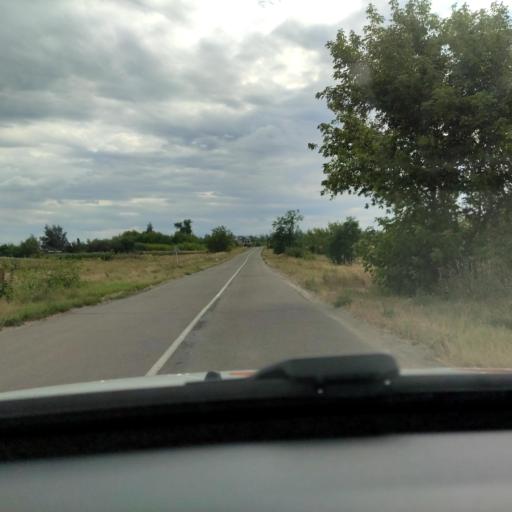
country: RU
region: Voronezj
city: Orlovo
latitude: 51.6637
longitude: 39.5743
